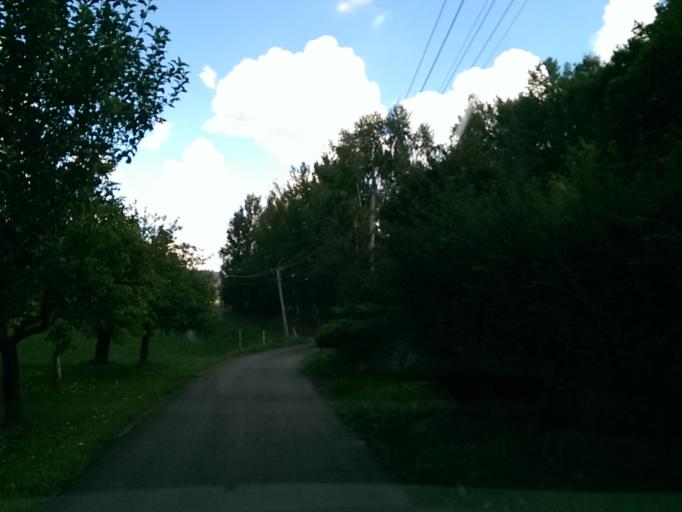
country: CZ
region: Liberecky
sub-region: Okres Semily
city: Turnov
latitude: 50.5463
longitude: 15.1329
